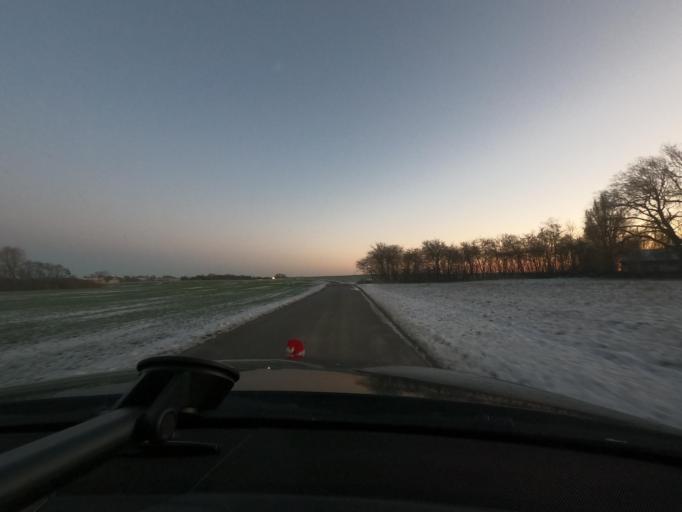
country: DK
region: South Denmark
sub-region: Sonderborg Kommune
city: Horuphav
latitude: 54.8689
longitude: 9.8970
